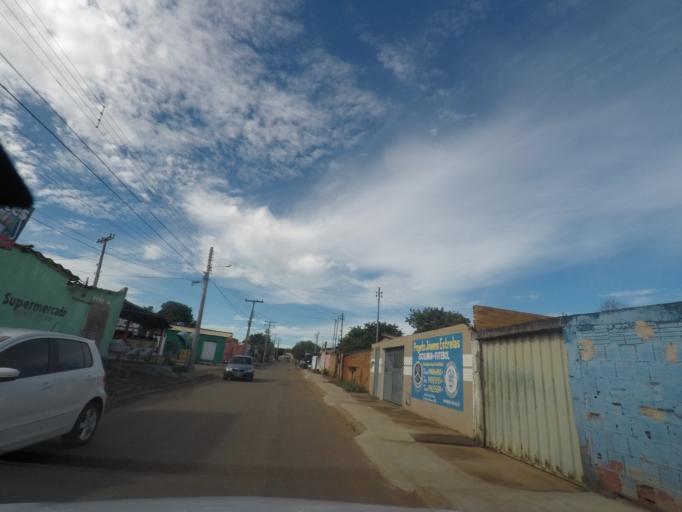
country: BR
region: Goias
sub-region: Aparecida De Goiania
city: Aparecida de Goiania
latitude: -16.8309
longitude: -49.2988
